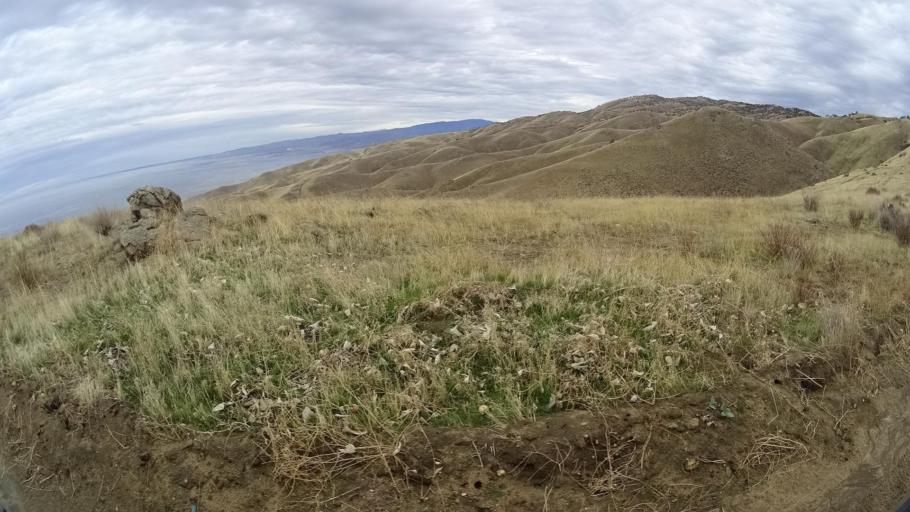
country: US
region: California
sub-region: Kern County
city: Arvin
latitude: 35.1306
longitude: -118.7706
